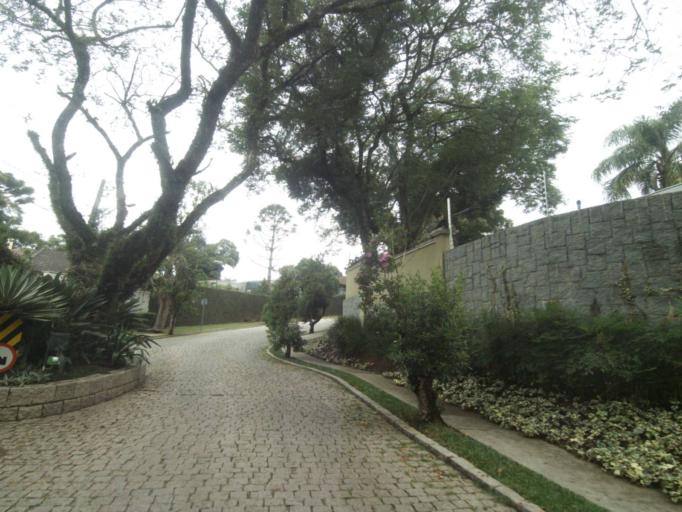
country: BR
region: Parana
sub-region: Curitiba
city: Curitiba
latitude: -25.4517
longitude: -49.3308
